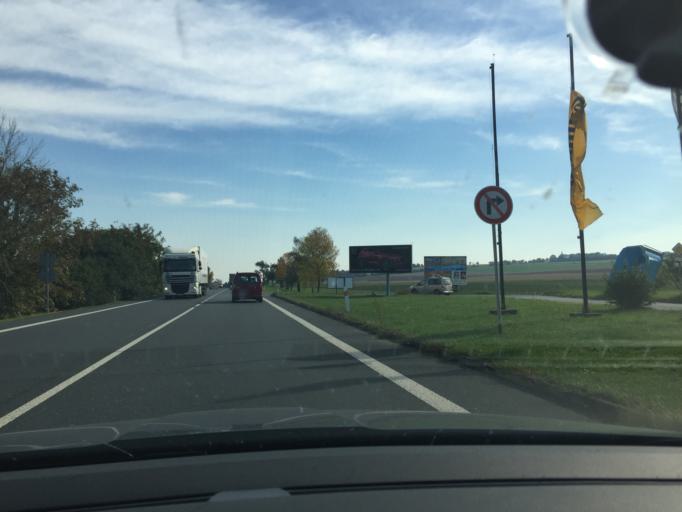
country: CZ
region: Central Bohemia
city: Velim
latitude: 50.0395
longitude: 15.1103
